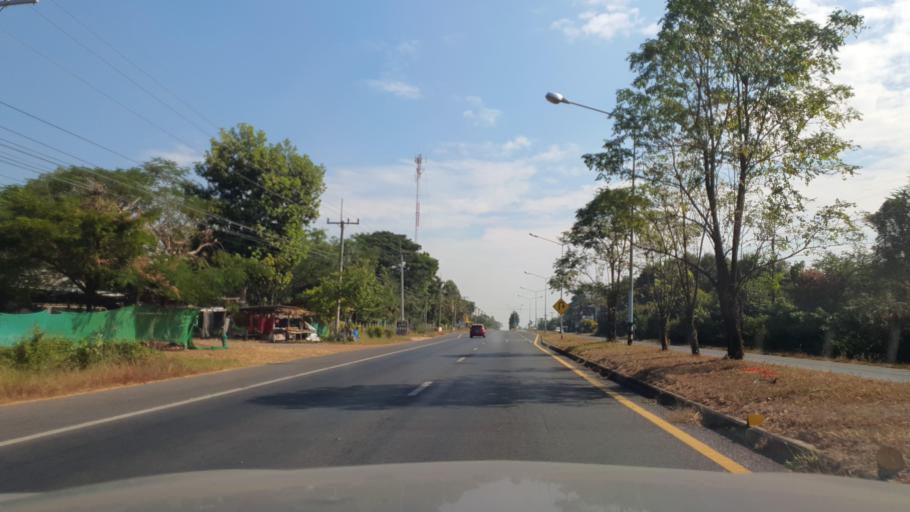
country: TH
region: Maha Sarakham
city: Kantharawichai
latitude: 16.3901
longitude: 103.2701
